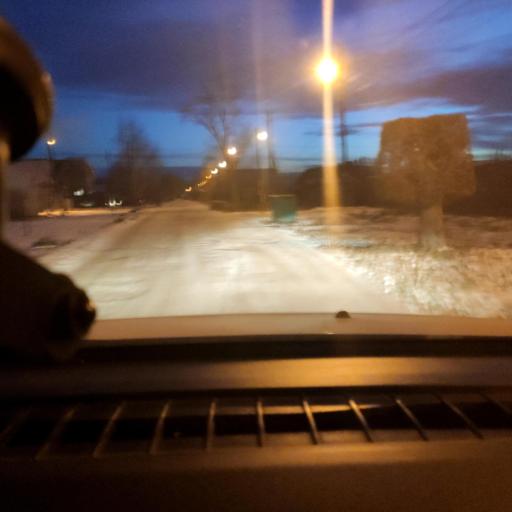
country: RU
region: Samara
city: Petra-Dubrava
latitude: 53.2574
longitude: 50.3342
